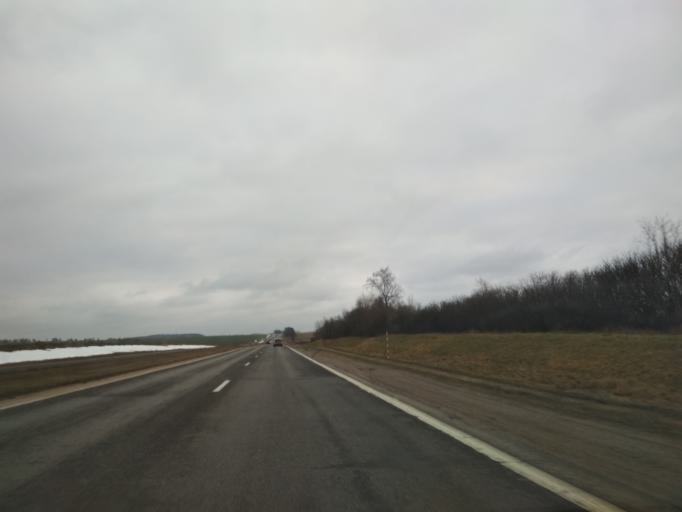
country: BY
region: Minsk
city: Blon'
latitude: 53.5624
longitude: 28.1456
